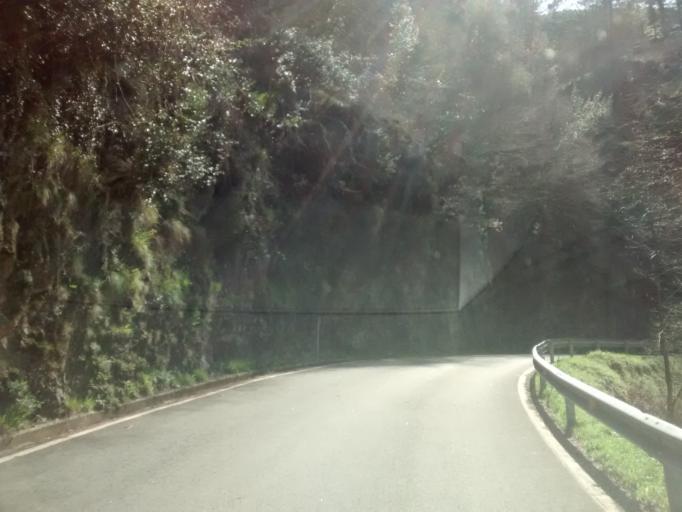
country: ES
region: Cantabria
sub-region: Provincia de Cantabria
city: Lierganes
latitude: 43.2832
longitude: -3.6976
